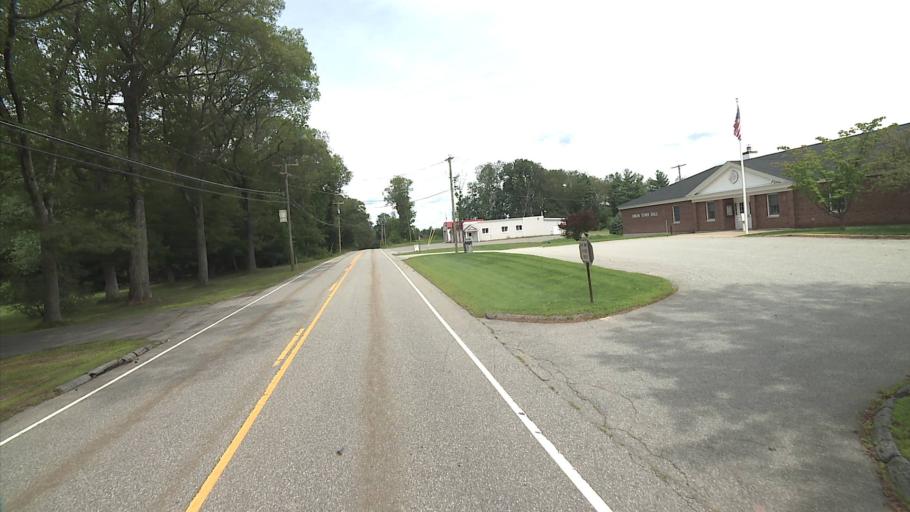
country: US
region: Massachusetts
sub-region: Hampden County
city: Holland
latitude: 41.9974
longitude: -72.1526
